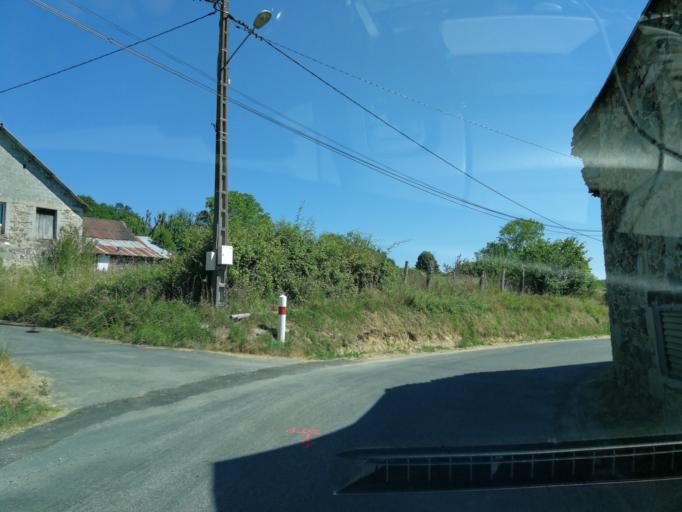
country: FR
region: Limousin
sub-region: Departement de la Correze
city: Sainte-Fereole
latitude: 45.2402
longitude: 1.5935
